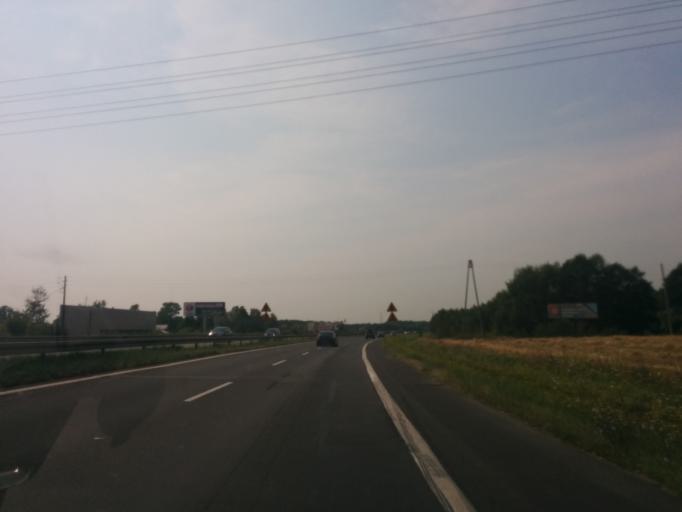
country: PL
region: Lodz Voivodeship
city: Zabia Wola
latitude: 52.0368
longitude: 20.6945
